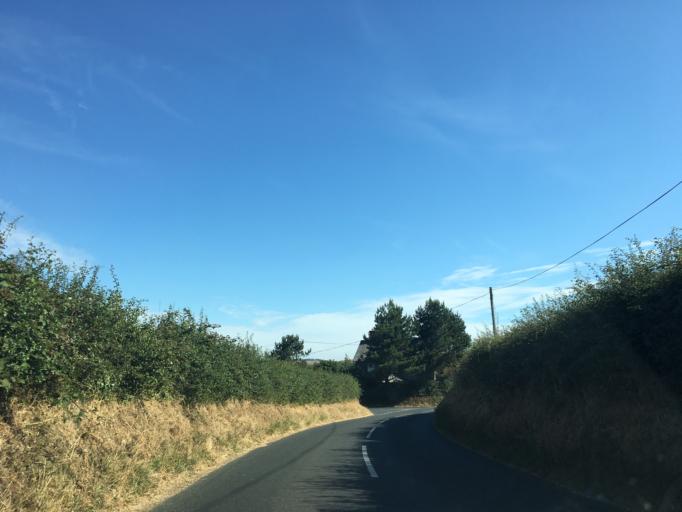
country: GB
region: England
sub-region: Isle of Wight
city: Chale
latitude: 50.6264
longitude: -1.3207
